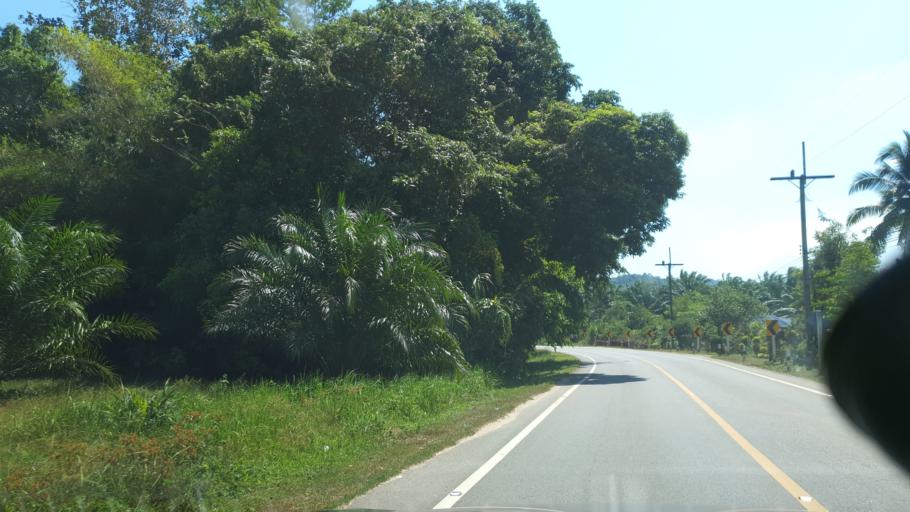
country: TH
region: Krabi
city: Khlong Thom
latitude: 7.9351
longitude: 99.2204
